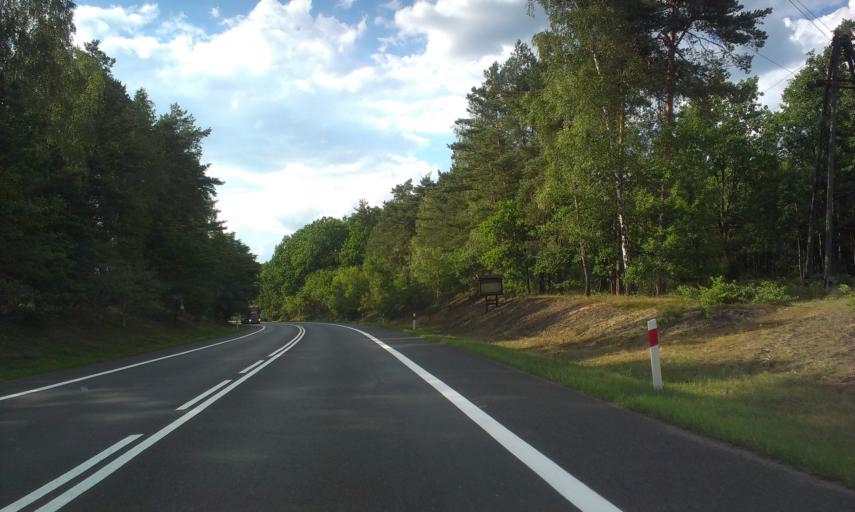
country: PL
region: Greater Poland Voivodeship
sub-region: Powiat pilski
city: Pila
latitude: 53.1796
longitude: 16.7736
